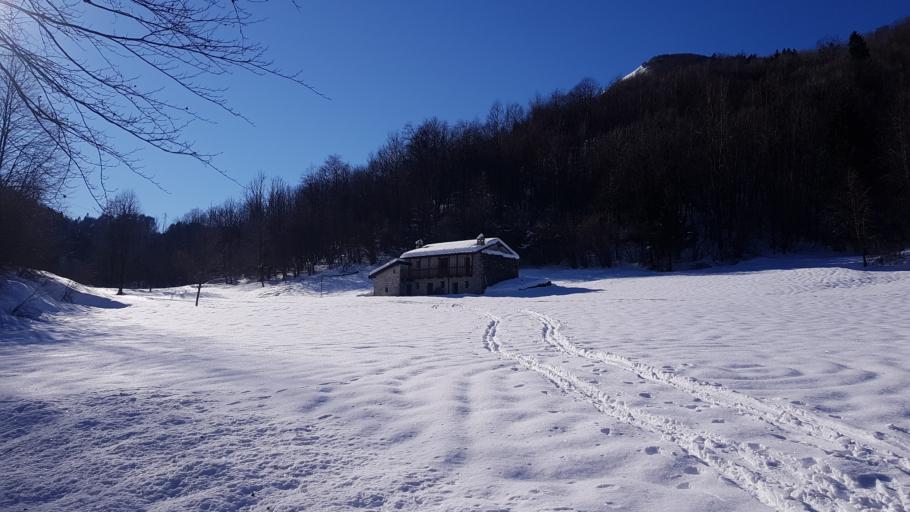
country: IT
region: Friuli Venezia Giulia
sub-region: Provincia di Udine
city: Trasaghis
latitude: 46.2805
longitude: 13.0172
